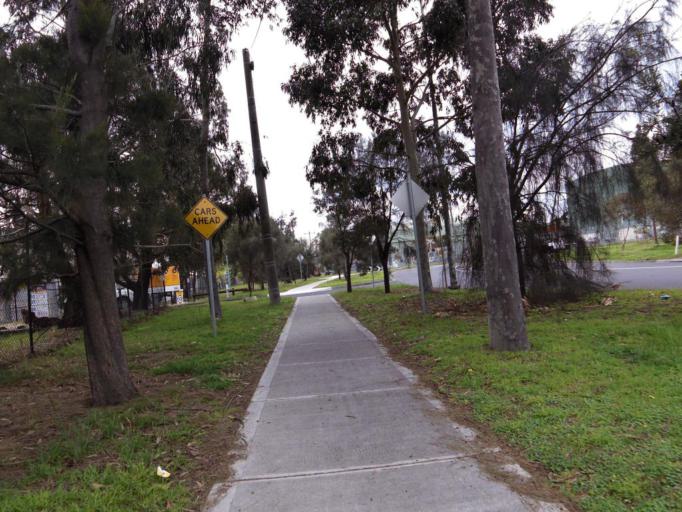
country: AU
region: Victoria
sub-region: Maribyrnong
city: Yarraville
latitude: -37.8228
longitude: 144.9102
